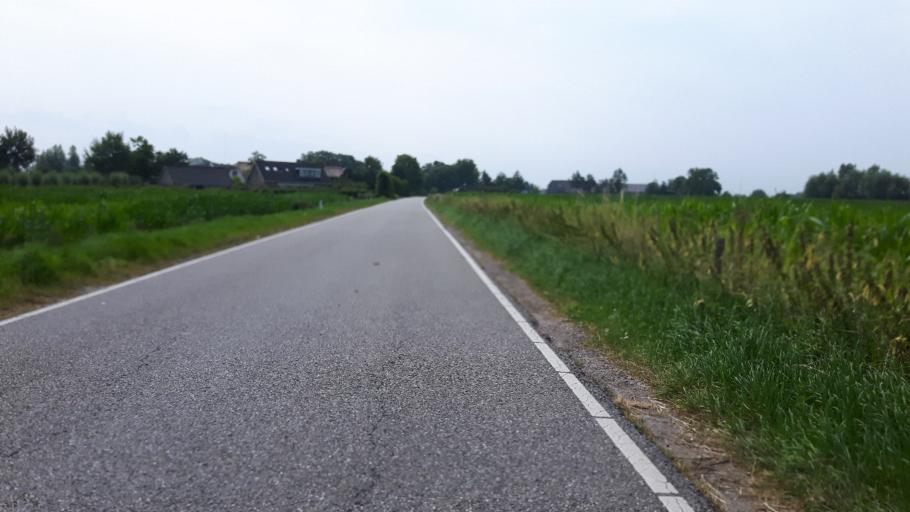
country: NL
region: Utrecht
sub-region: Gemeente IJsselstein
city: IJsselstein
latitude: 52.0508
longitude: 5.0187
